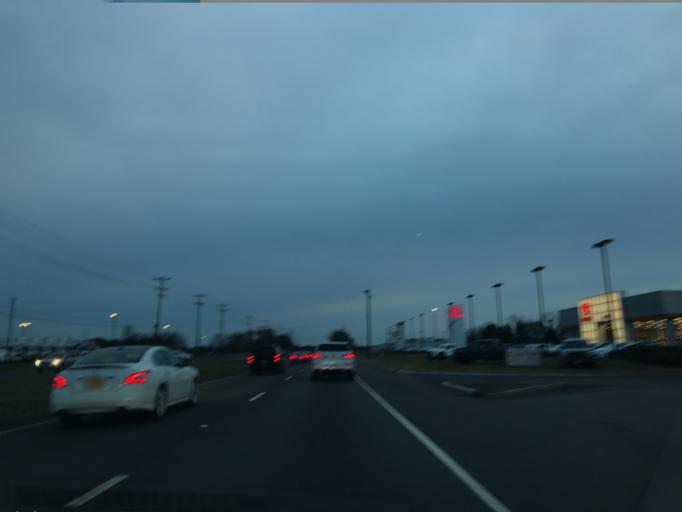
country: US
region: New Jersey
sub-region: Middlesex County
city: Dayton
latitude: 40.3770
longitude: -74.5012
